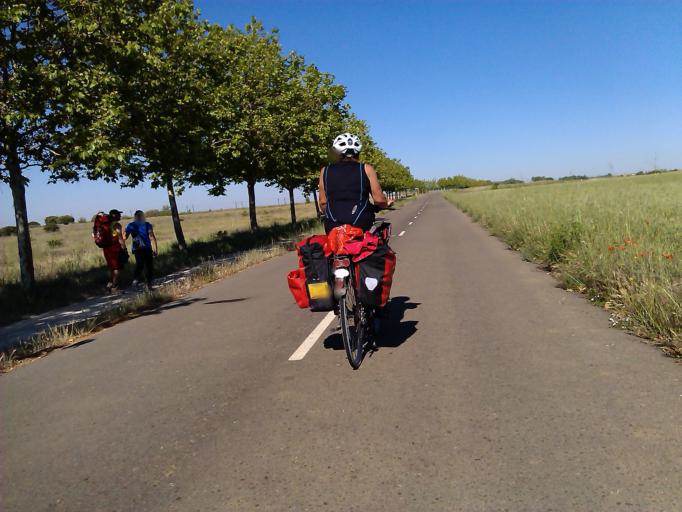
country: ES
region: Castille and Leon
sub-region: Provincia de Leon
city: Calzada del Coto
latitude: 42.3839
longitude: -5.0947
